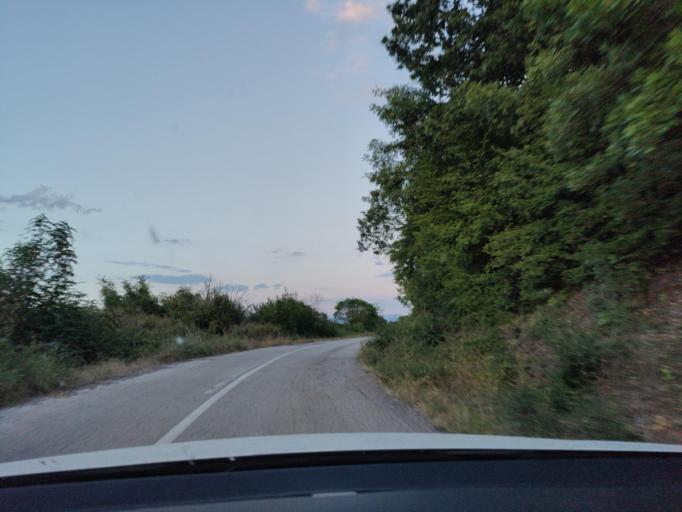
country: GR
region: Central Macedonia
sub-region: Nomos Serron
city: Chrysochorafa
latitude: 41.1805
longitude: 23.1457
